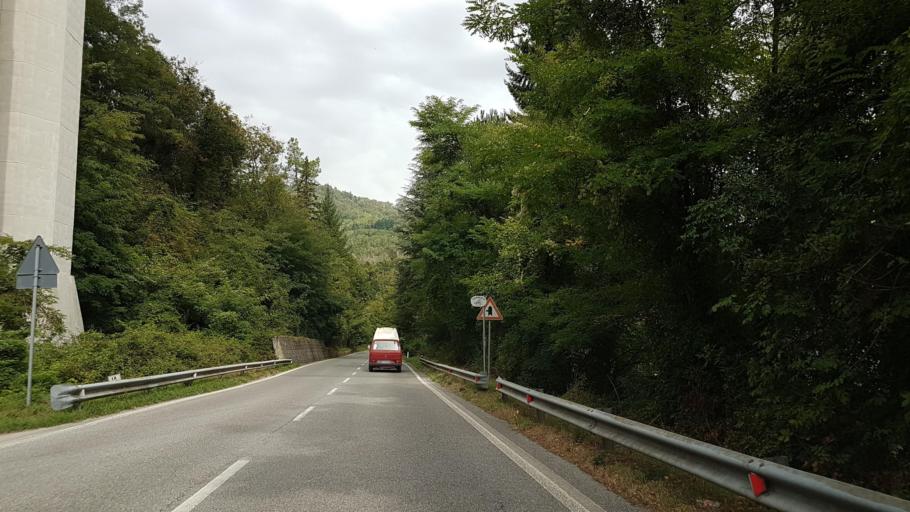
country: IT
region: Liguria
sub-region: Provincia di La Spezia
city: Carrodano
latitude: 44.2329
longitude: 9.6393
